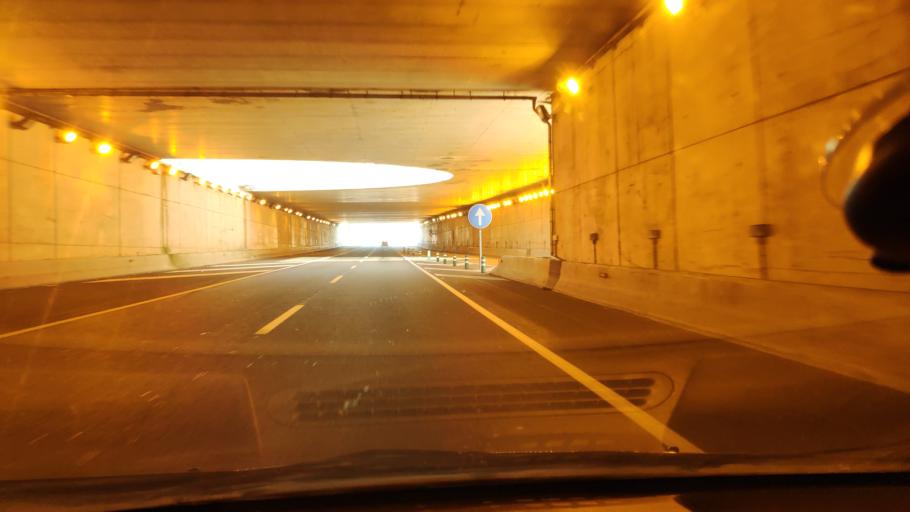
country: ES
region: Catalonia
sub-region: Provincia de Barcelona
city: Sant Quirze del Valles
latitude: 41.5621
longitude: 2.0778
